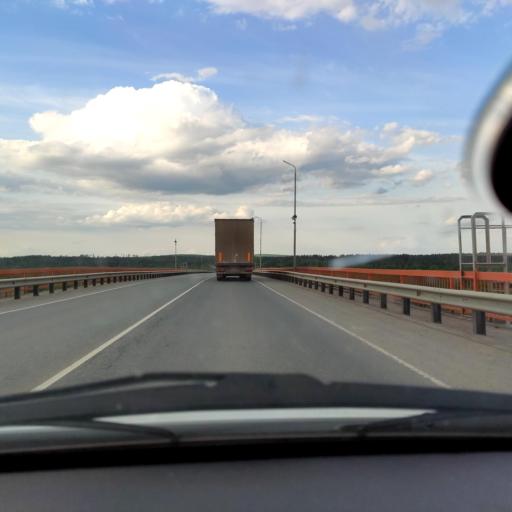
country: RU
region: Bashkortostan
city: Dyurtyuli
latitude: 55.5301
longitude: 54.8496
